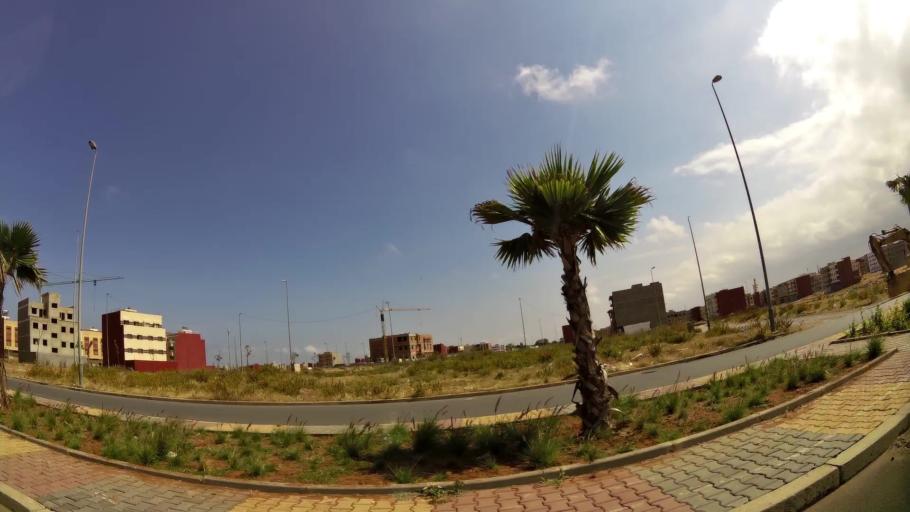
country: MA
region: Rabat-Sale-Zemmour-Zaer
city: Sale
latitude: 34.0741
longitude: -6.7712
